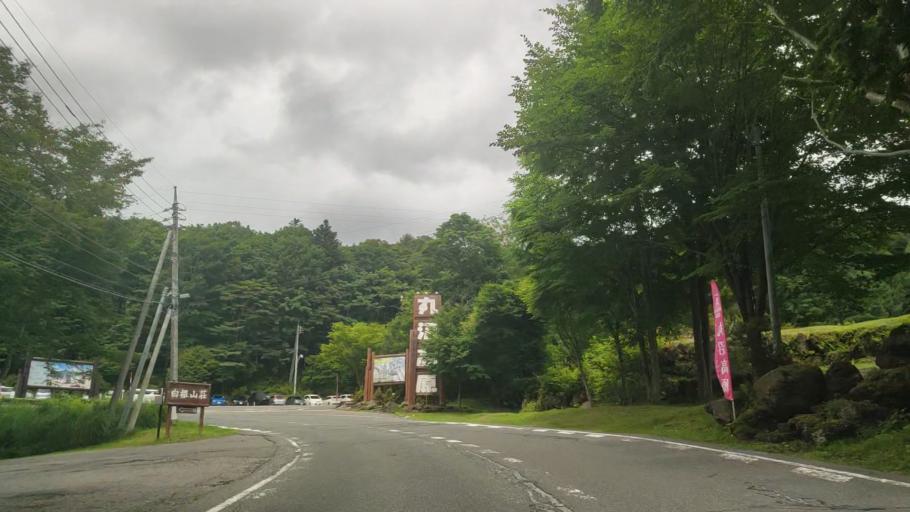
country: JP
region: Tochigi
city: Nikko
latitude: 36.8154
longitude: 139.3290
